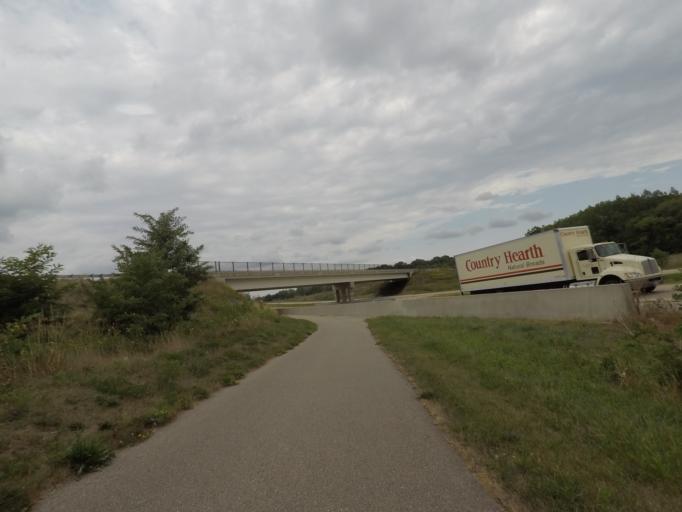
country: US
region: Wisconsin
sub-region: Jefferson County
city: Lake Koshkonong
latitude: 42.8821
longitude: -88.8786
